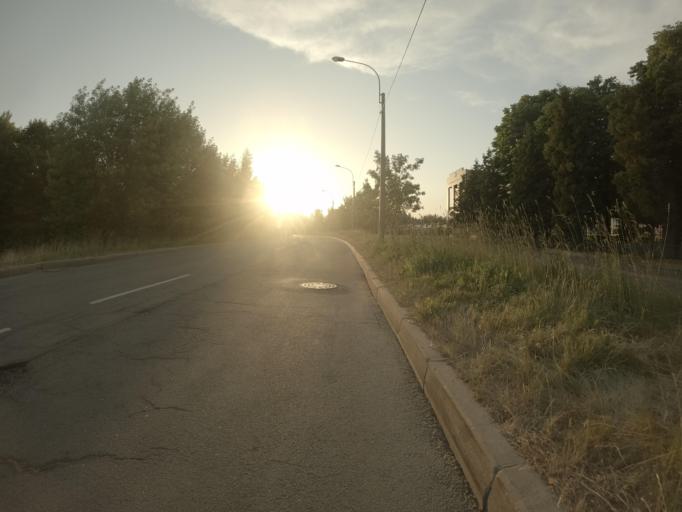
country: RU
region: St.-Petersburg
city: Krasnogvargeisky
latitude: 59.9328
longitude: 30.4280
